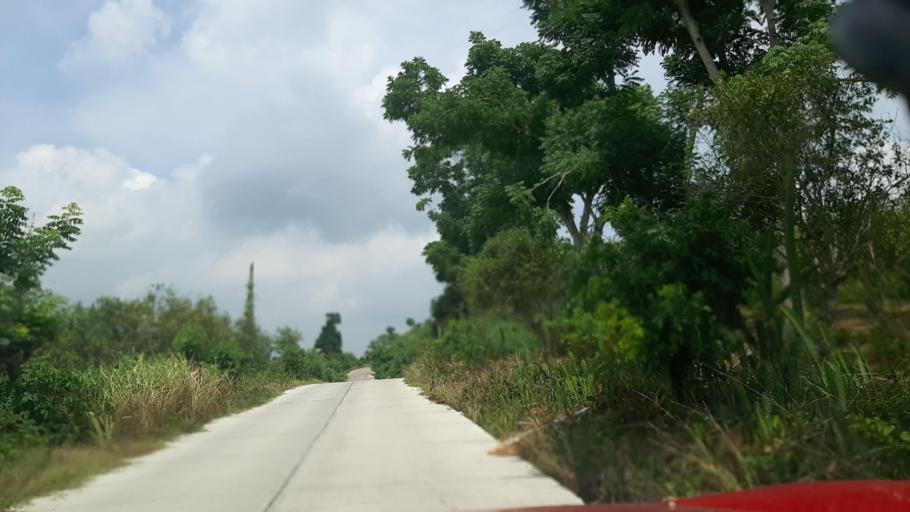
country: MX
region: Veracruz
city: Gutierrez Zamora
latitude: 20.4446
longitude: -97.1691
